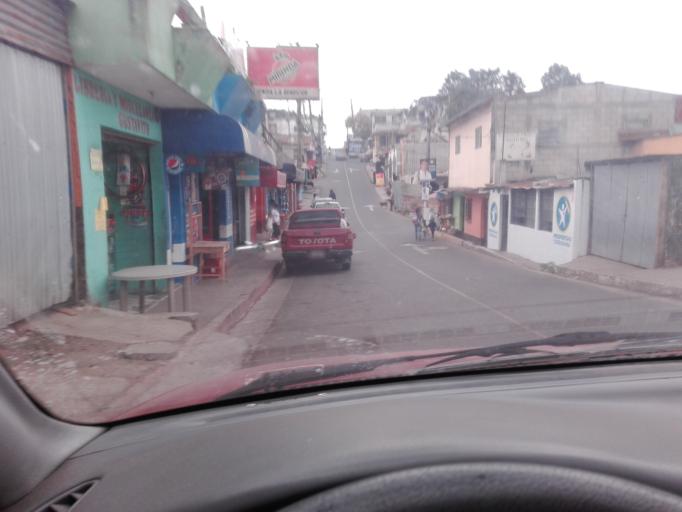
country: GT
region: Guatemala
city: San Jose Pinula
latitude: 14.5709
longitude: -90.4453
